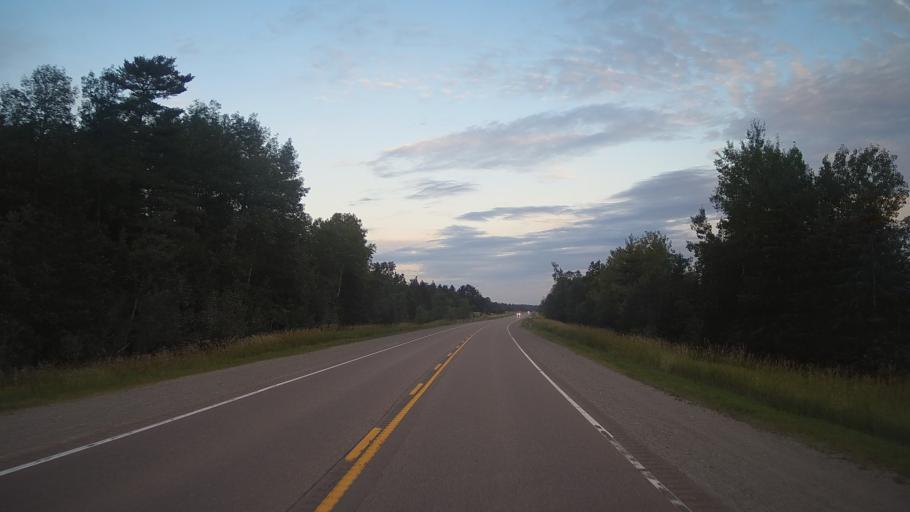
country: CA
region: Ontario
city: Pembroke
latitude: 45.7910
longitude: -77.1107
